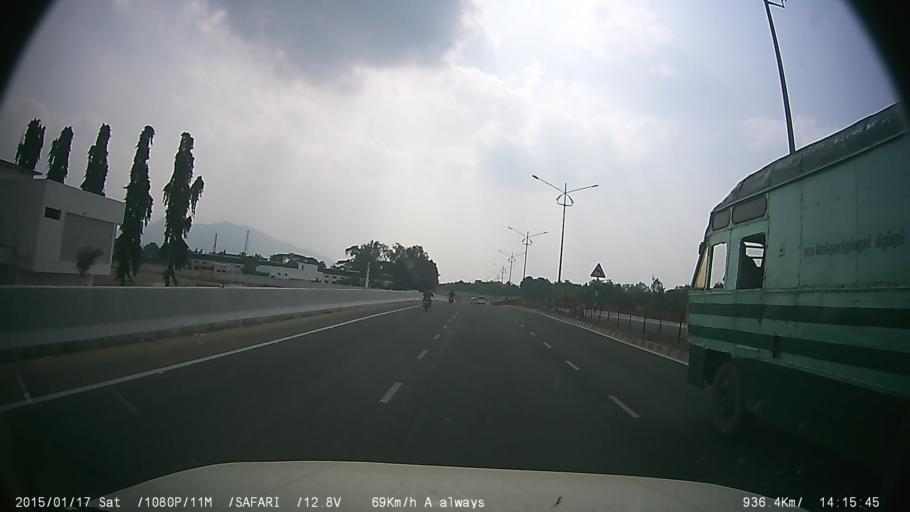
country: IN
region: Tamil Nadu
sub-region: Vellore
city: Ambur
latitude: 12.7634
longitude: 78.7040
